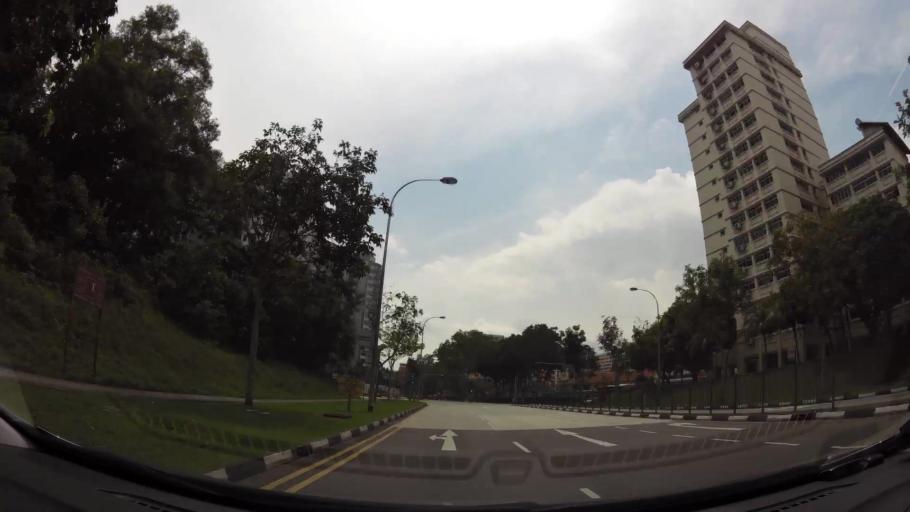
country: MY
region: Johor
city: Kampung Pasir Gudang Baru
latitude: 1.3820
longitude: 103.9391
